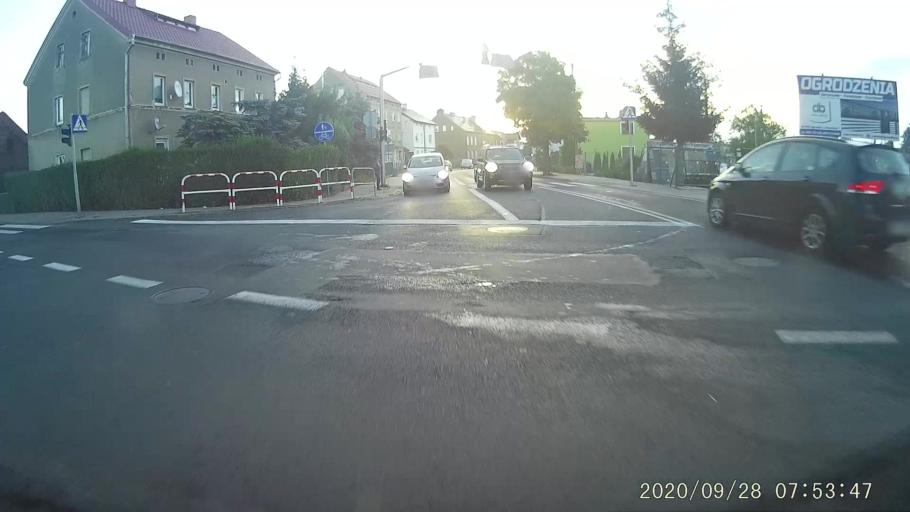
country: PL
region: Lower Silesian Voivodeship
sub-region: Powiat zgorzelecki
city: Bogatynia
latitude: 50.9104
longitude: 14.9656
